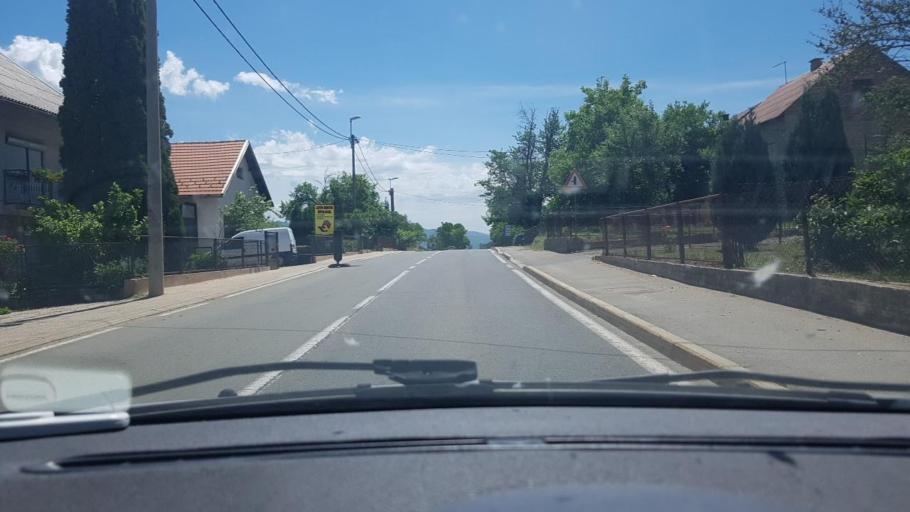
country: HR
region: Licko-Senjska
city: Otocac
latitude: 44.8620
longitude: 15.2627
